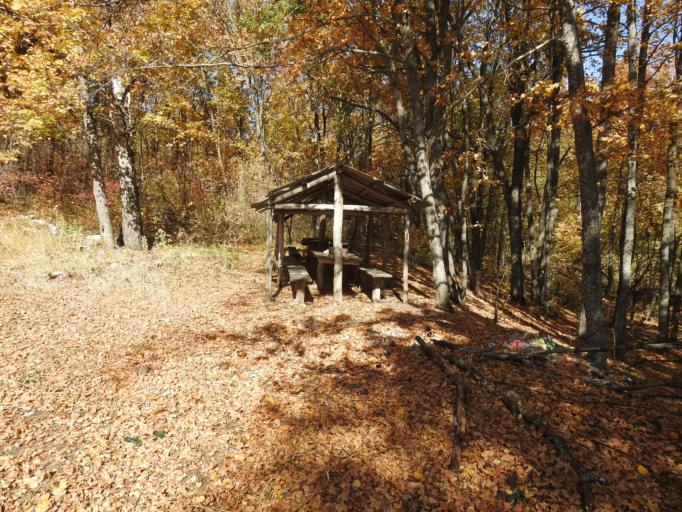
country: RU
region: Saratov
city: Baltay
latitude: 52.4840
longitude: 46.7217
